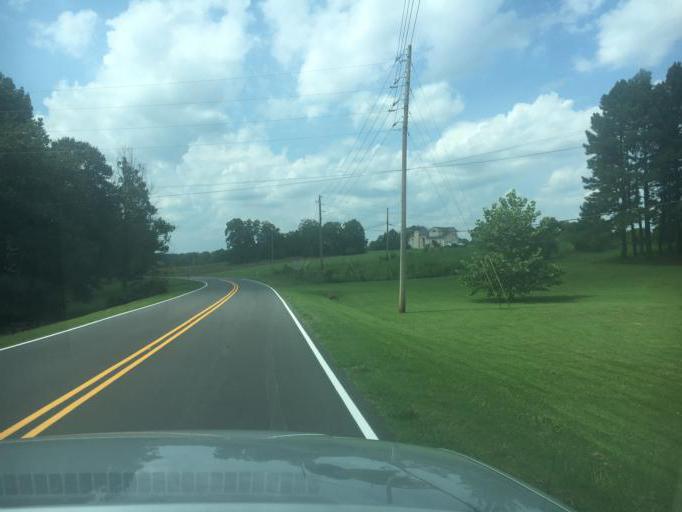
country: US
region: North Carolina
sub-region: Gaston County
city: Cherryville
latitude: 35.4121
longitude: -81.4045
